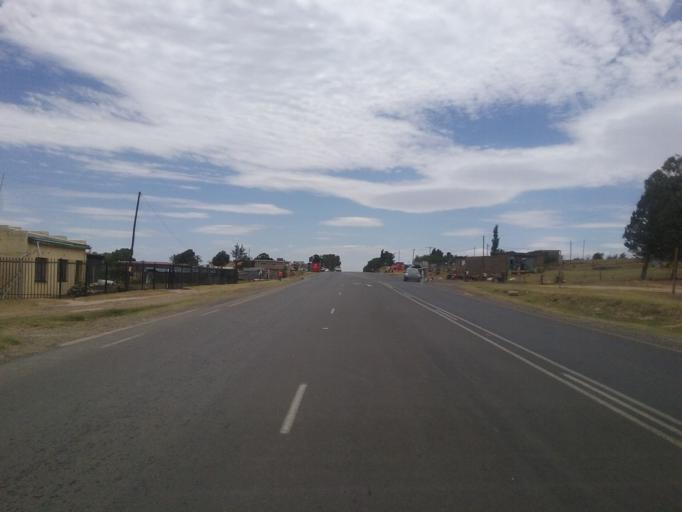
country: LS
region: Maseru
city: Maseru
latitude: -29.4901
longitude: 27.5273
